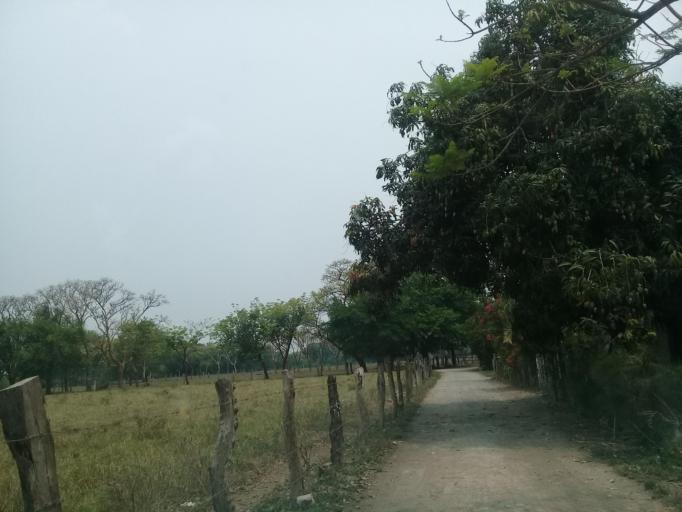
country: MX
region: Veracruz
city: Jamapa
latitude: 18.9548
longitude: -96.2058
